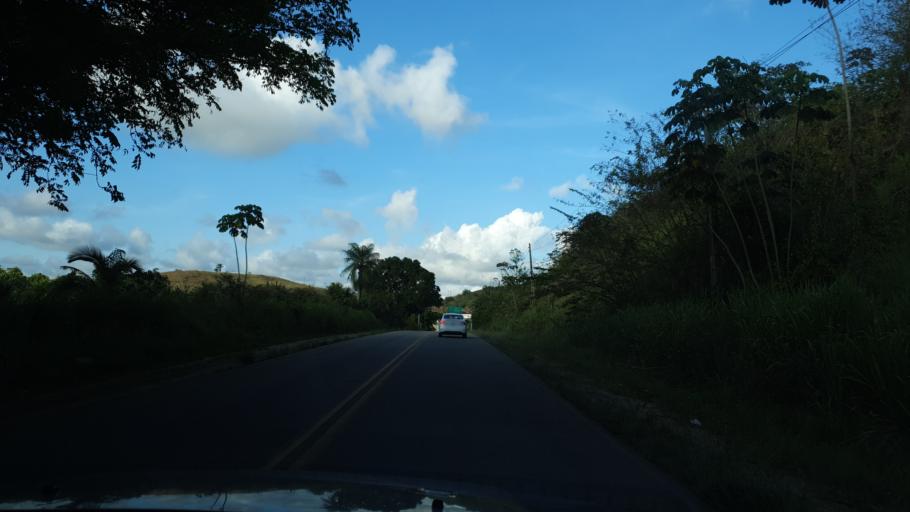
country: BR
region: Pernambuco
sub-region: Barreiros
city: Barreiros
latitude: -8.7940
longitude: -35.1876
